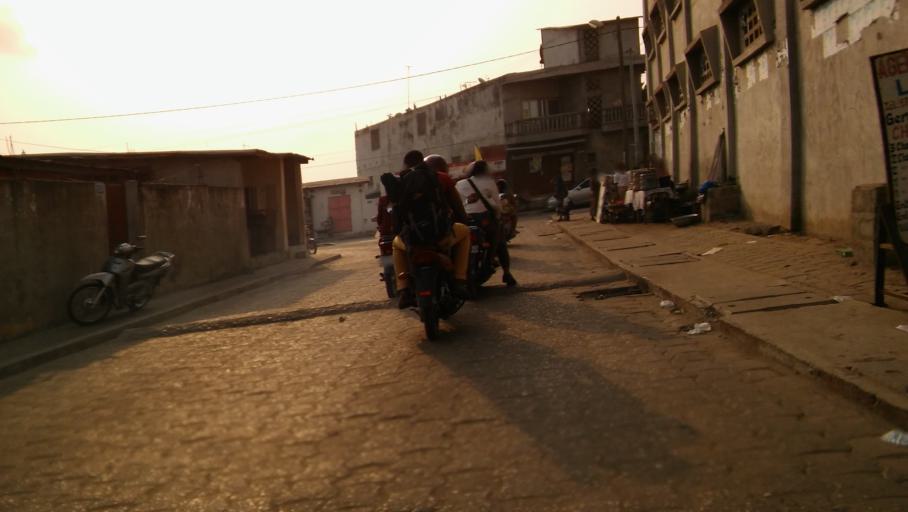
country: BJ
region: Littoral
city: Cotonou
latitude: 6.3847
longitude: 2.3858
